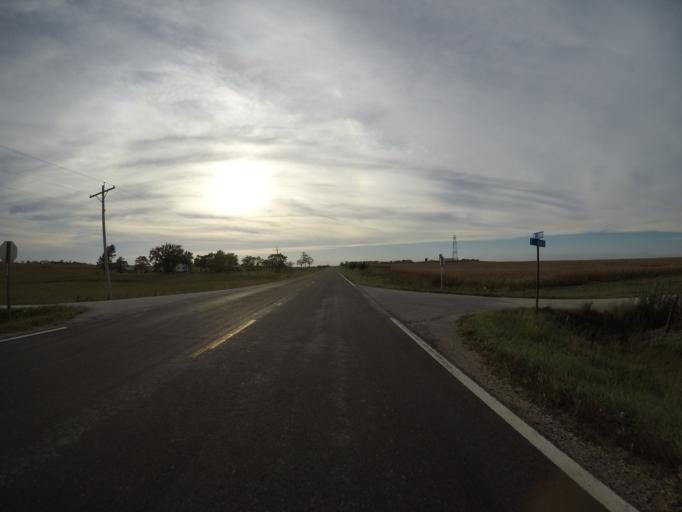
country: US
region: Kansas
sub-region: Osage County
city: Overbrook
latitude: 38.7825
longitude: -95.4275
